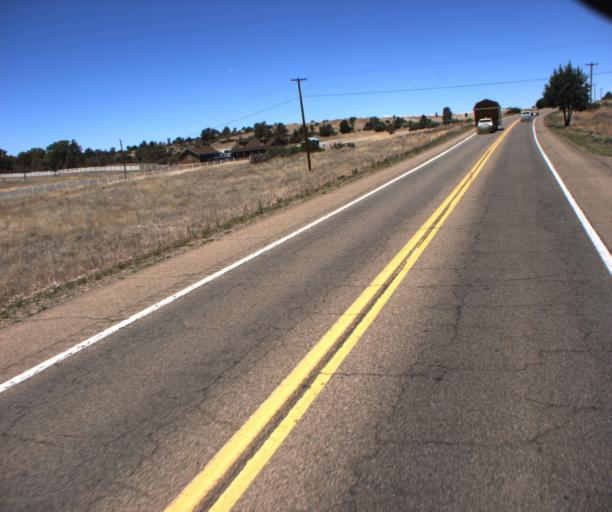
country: US
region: Arizona
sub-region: Yavapai County
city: Prescott
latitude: 34.6228
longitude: -112.4260
